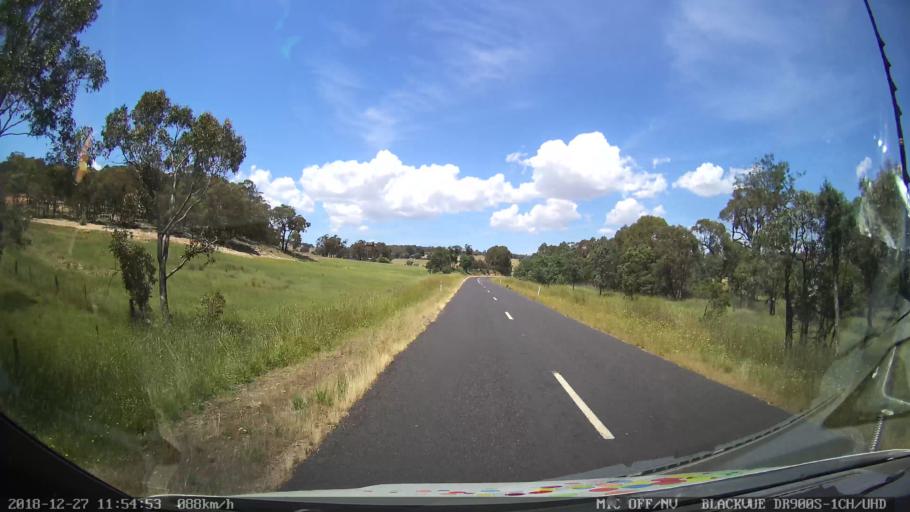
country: AU
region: New South Wales
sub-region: Blayney
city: Blayney
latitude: -33.6807
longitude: 149.4013
